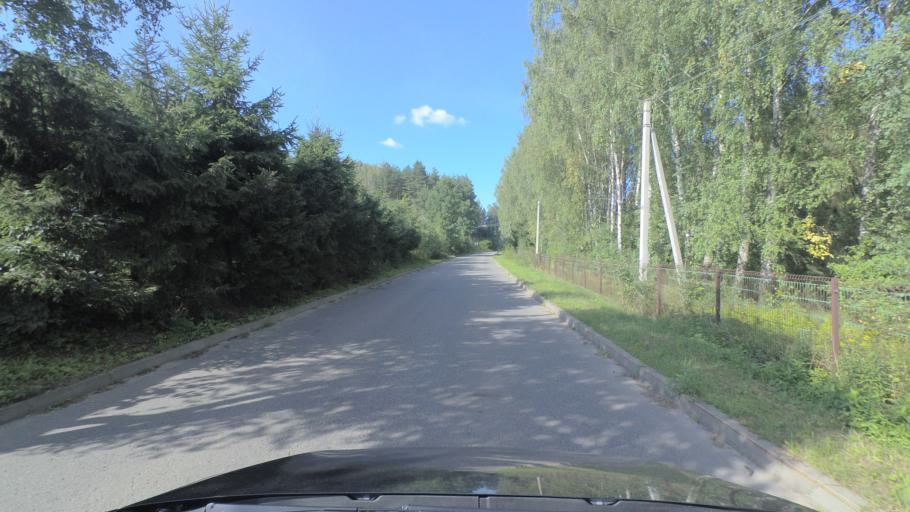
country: LT
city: Nemencine
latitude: 54.8422
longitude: 25.3712
